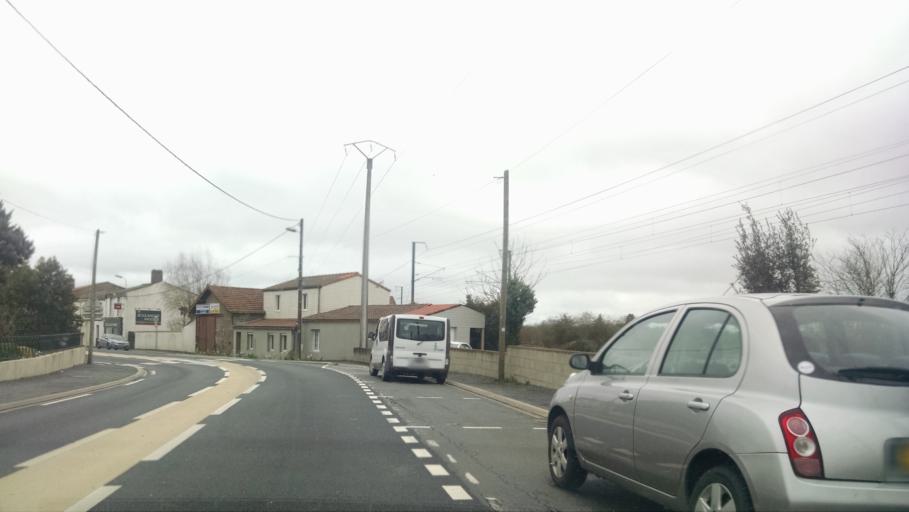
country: FR
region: Pays de la Loire
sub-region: Departement de la Loire-Atlantique
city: Le Pallet
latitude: 47.1422
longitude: -1.3427
